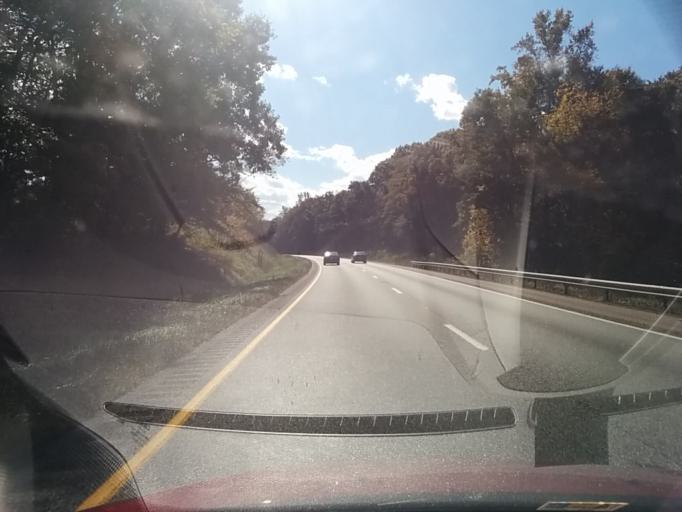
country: US
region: Virginia
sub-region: Rockbridge County
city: East Lexington
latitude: 37.8505
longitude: -79.3619
